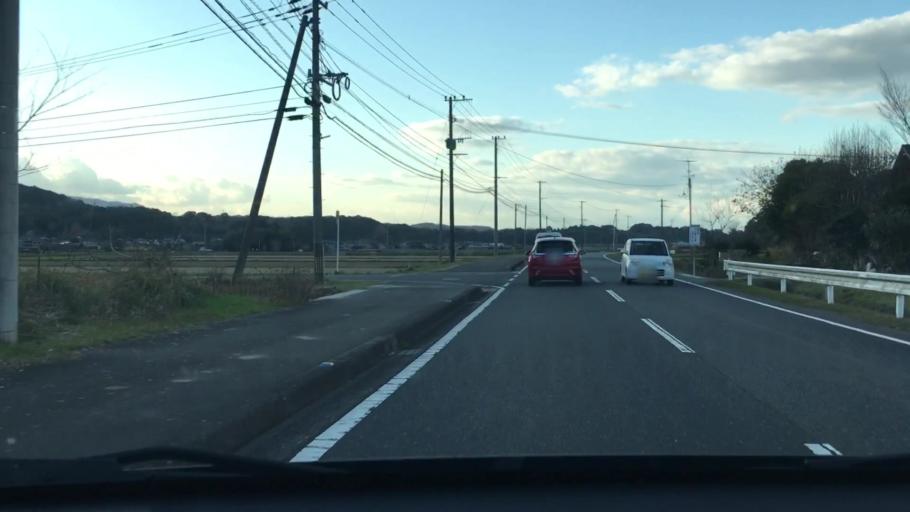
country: JP
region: Oita
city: Bungo-Takada-shi
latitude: 33.5042
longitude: 131.3655
